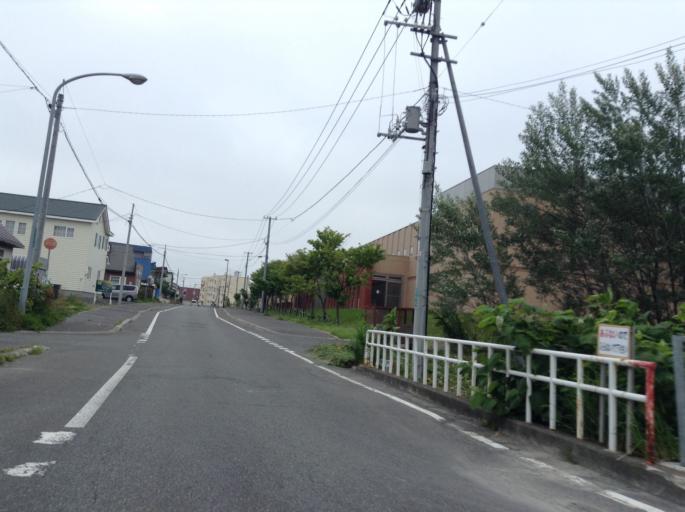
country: JP
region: Hokkaido
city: Wakkanai
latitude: 45.3960
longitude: 141.6893
